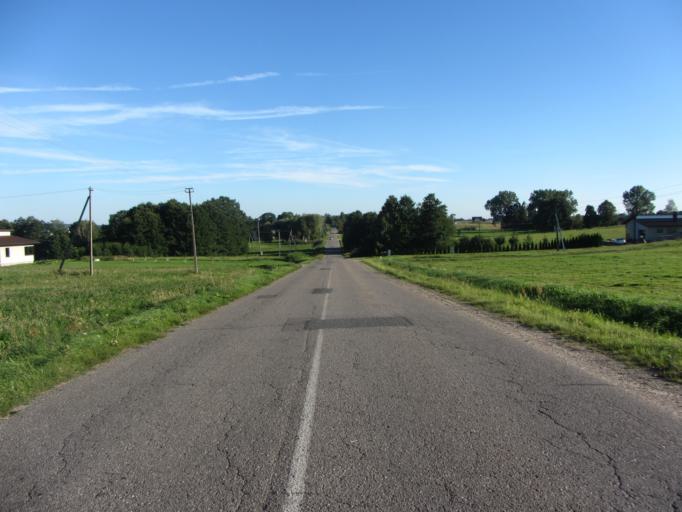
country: LT
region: Alytaus apskritis
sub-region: Alytus
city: Alytus
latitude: 54.4796
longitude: 24.0348
